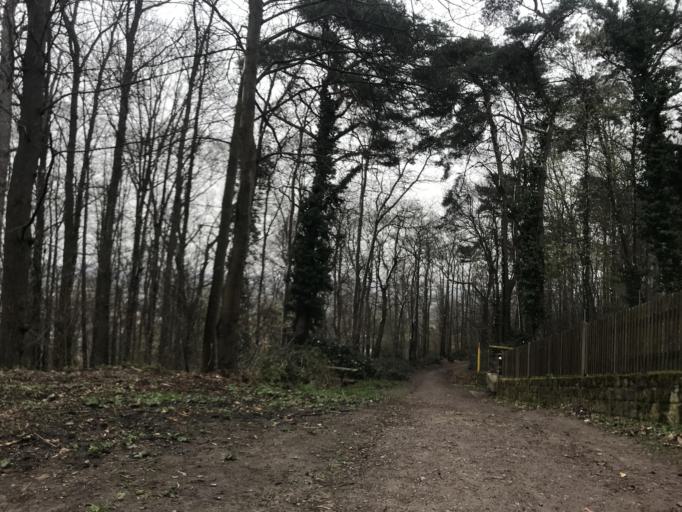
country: DE
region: Rheinland-Pfalz
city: Neustadt
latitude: 49.3464
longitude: 8.1282
